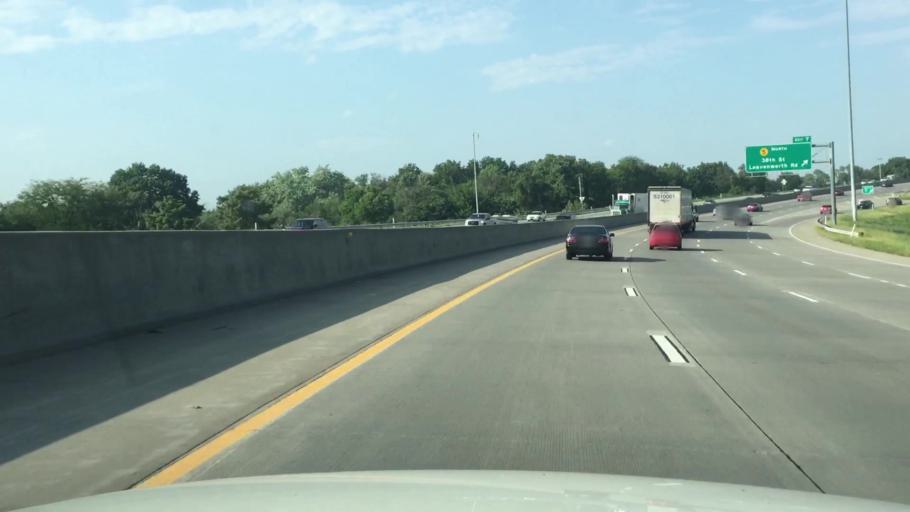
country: US
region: Kansas
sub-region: Wyandotte County
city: Kansas City
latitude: 39.1383
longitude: -94.6755
